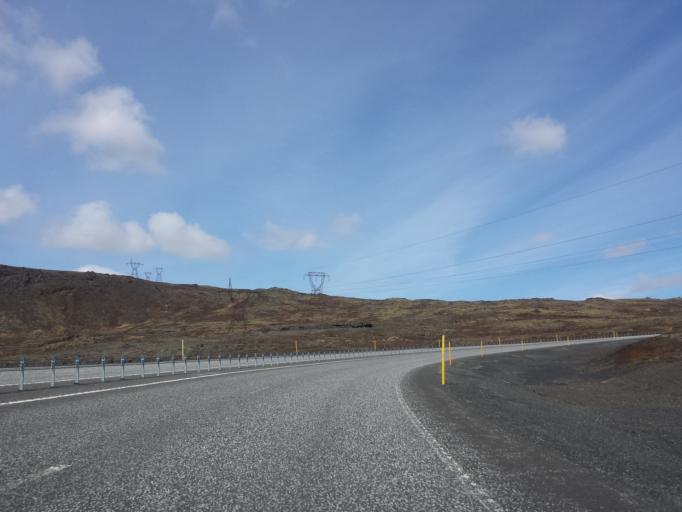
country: IS
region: South
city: Hveragerdi
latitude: 64.0013
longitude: -21.2253
